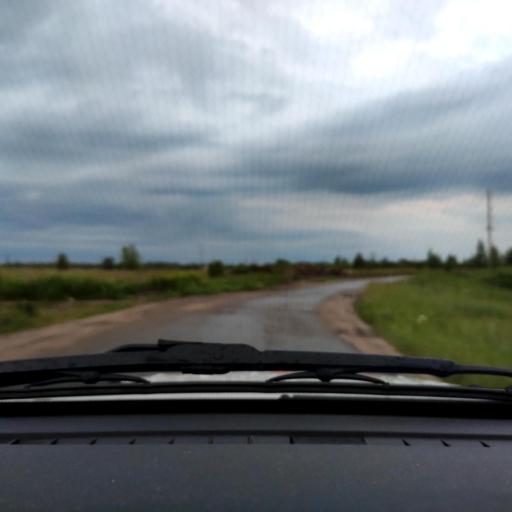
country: RU
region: Voronezj
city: Maslovka
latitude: 51.5166
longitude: 39.2264
